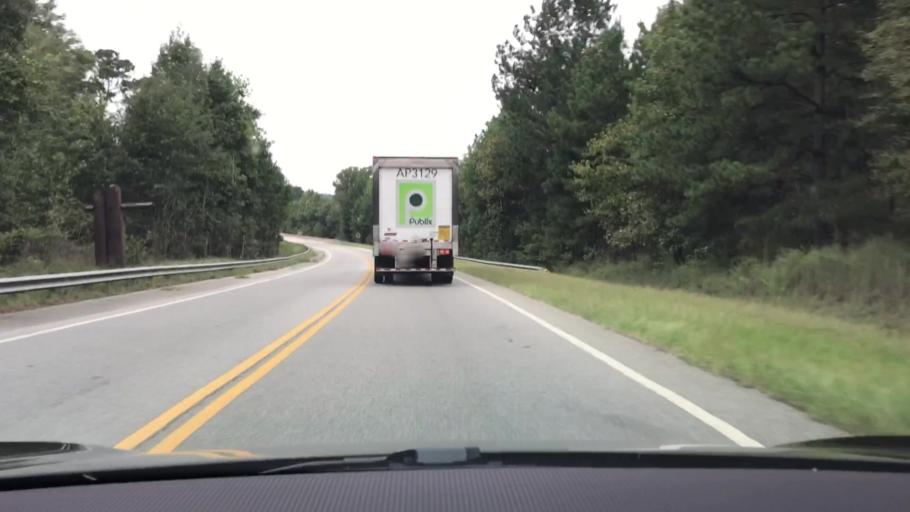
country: US
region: Georgia
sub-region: Greene County
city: Greensboro
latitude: 33.7185
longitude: -83.2931
